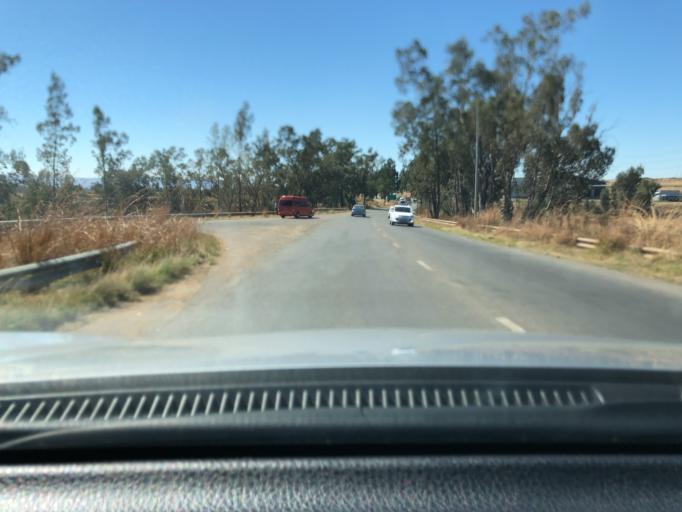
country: ZA
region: KwaZulu-Natal
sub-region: Amajuba District Municipality
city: Newcastle
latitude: -27.7620
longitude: 29.9563
